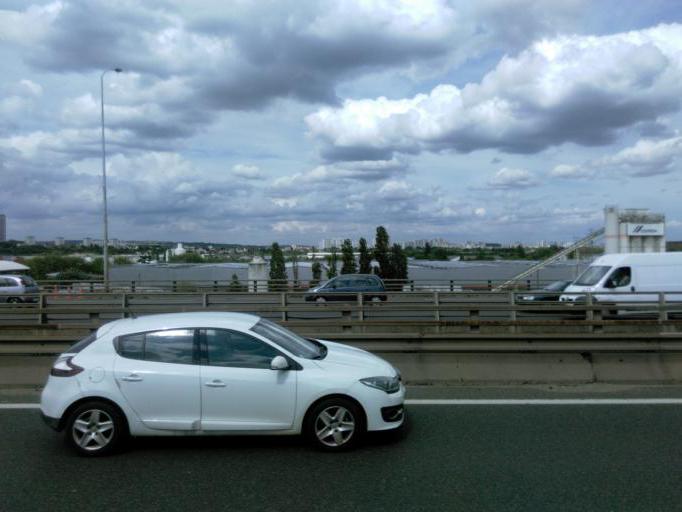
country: FR
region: Ile-de-France
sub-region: Departement des Hauts-de-Seine
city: Gennevilliers
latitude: 48.9417
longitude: 2.2907
